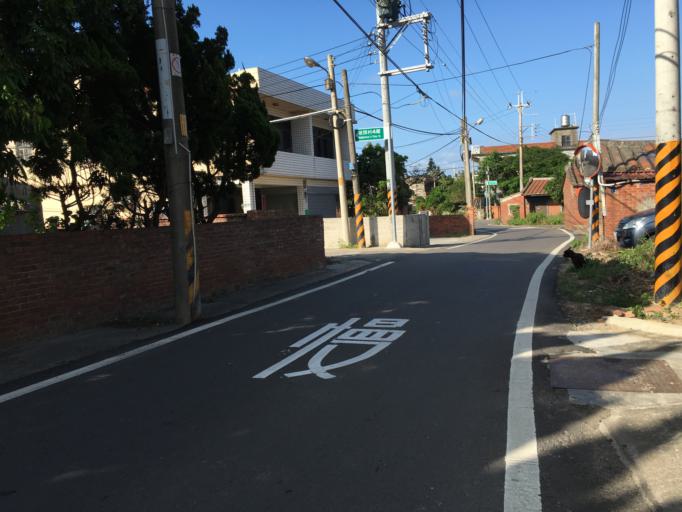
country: TW
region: Taiwan
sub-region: Hsinchu
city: Zhubei
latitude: 24.9247
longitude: 120.9840
